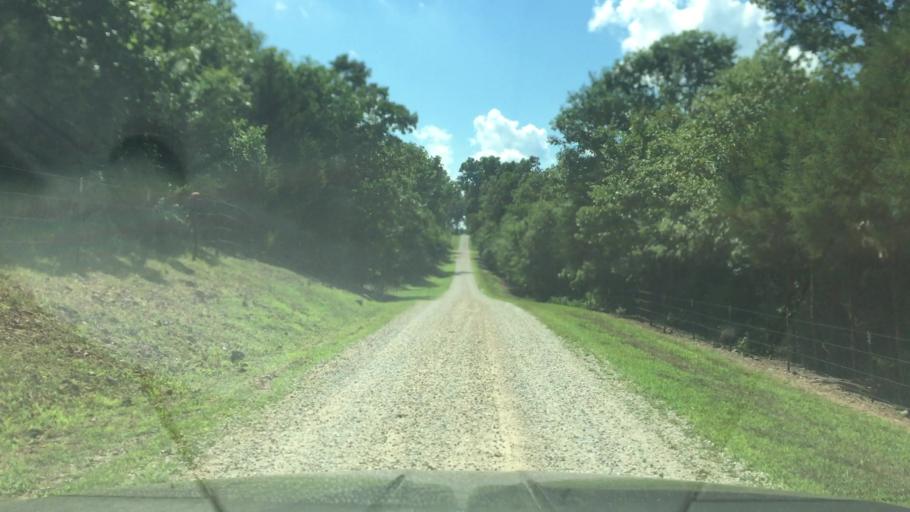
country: US
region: Missouri
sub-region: Miller County
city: Tuscumbia
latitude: 38.1310
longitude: -92.4471
